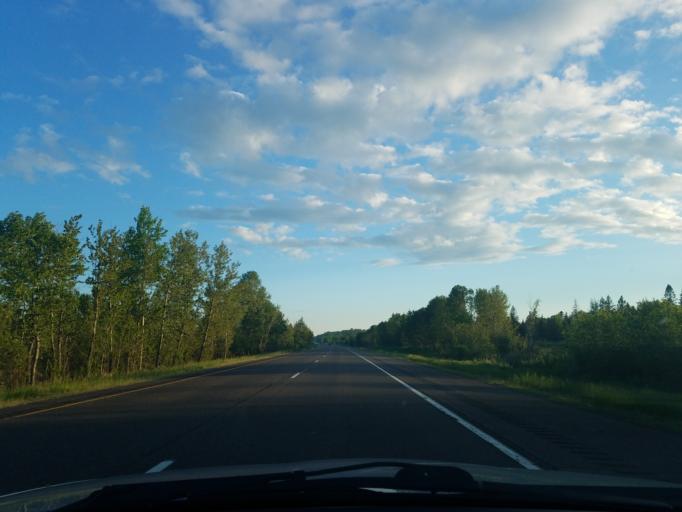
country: US
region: Minnesota
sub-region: Carlton County
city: Carlton
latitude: 46.6066
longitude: -92.5607
